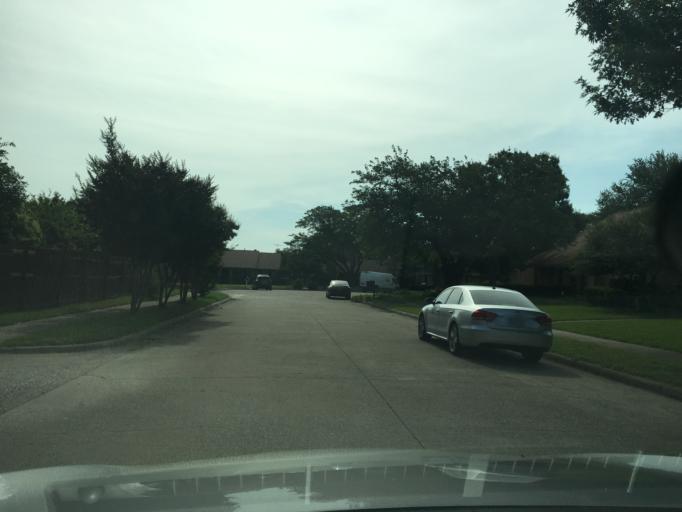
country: US
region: Texas
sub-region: Dallas County
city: Richardson
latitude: 32.9668
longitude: -96.6802
